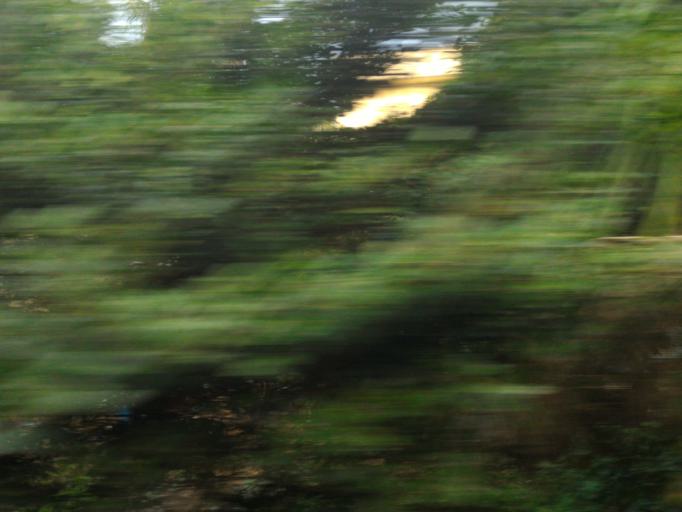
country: TW
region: Taiwan
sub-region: Taoyuan
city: Taoyuan
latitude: 24.9799
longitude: 121.3295
